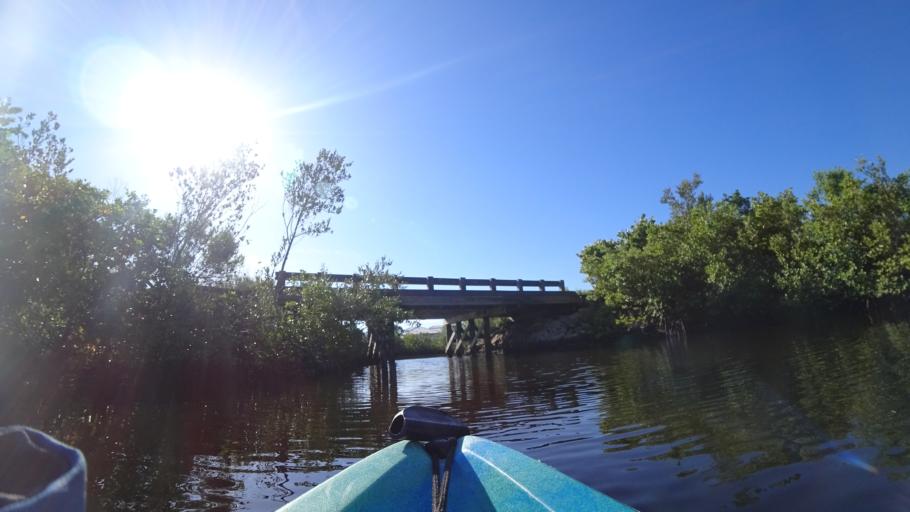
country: US
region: Florida
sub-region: Manatee County
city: Cortez
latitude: 27.5013
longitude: -82.6652
